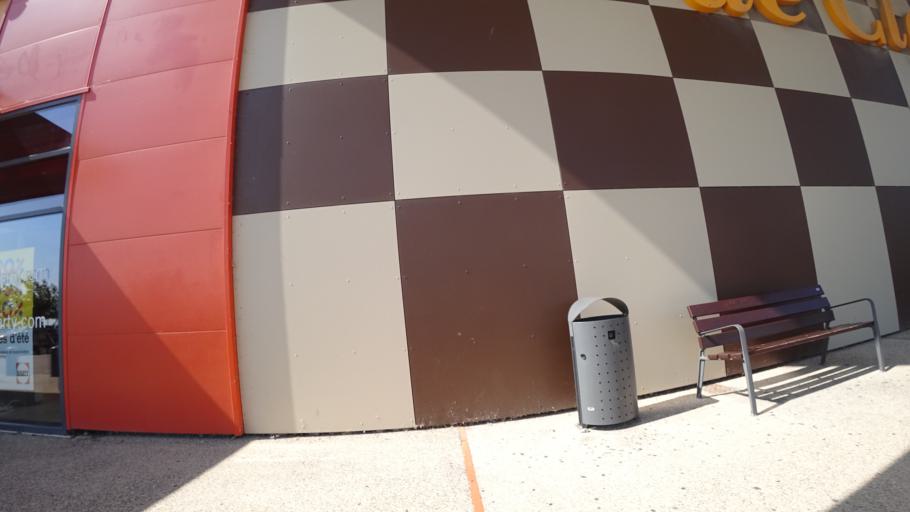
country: FR
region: Languedoc-Roussillon
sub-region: Departement des Pyrenees-Orientales
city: Pia
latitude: 42.7715
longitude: 2.9159
